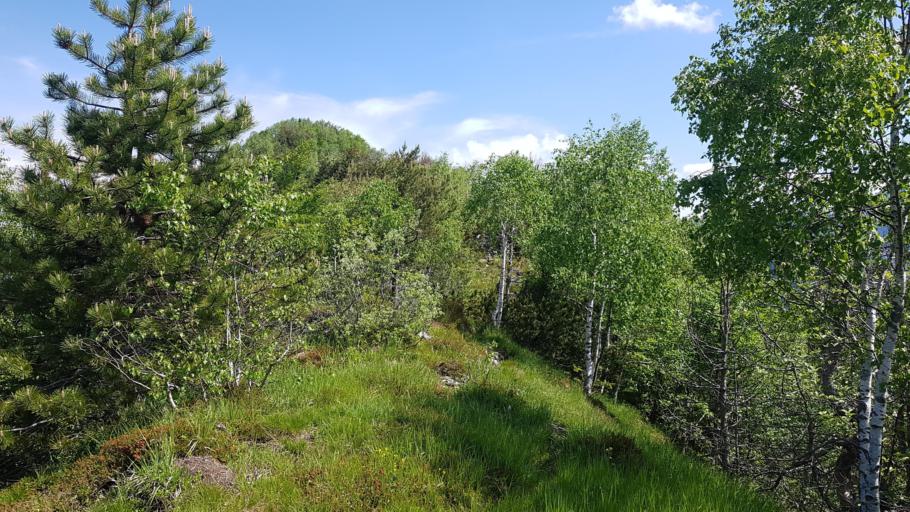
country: IT
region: Friuli Venezia Giulia
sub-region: Provincia di Udine
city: Moggio di Sotto
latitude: 46.4313
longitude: 13.1818
